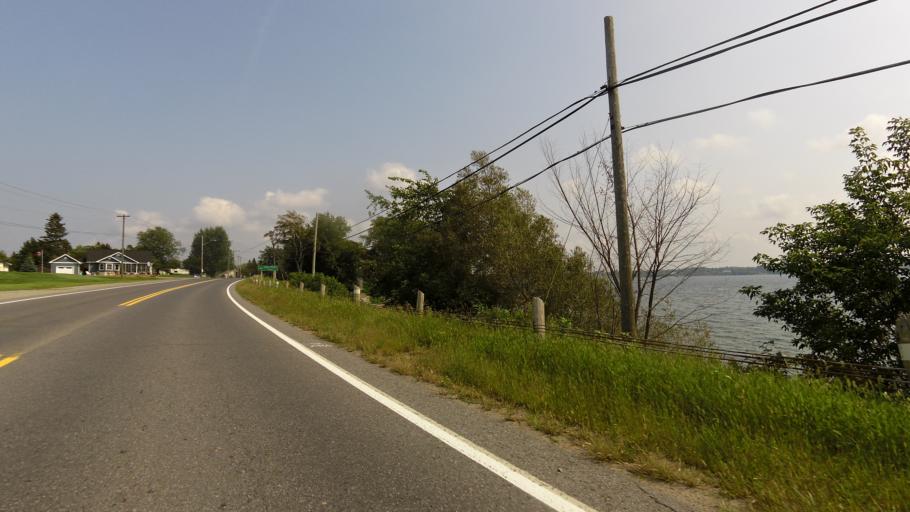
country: CA
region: Ontario
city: Prescott
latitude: 44.6988
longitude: -75.5359
